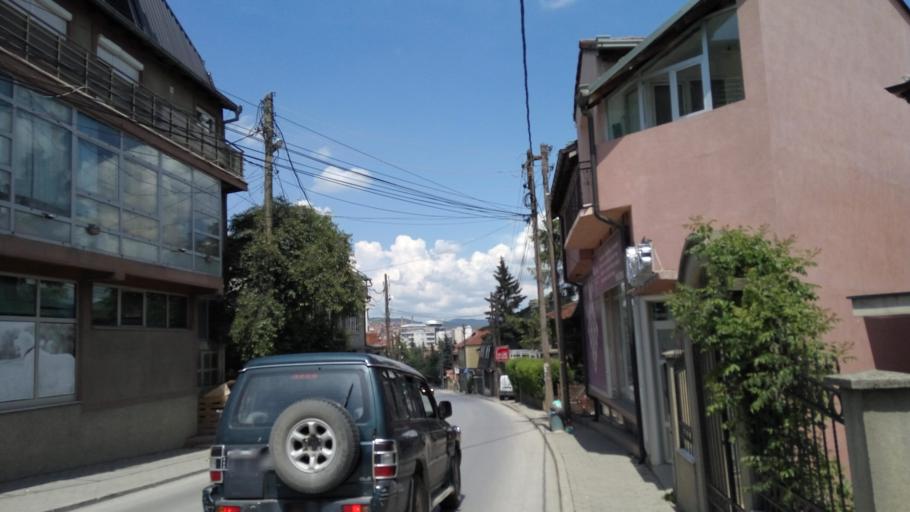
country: XK
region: Pristina
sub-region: Komuna e Prishtines
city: Pristina
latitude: 42.6618
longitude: 21.1521
